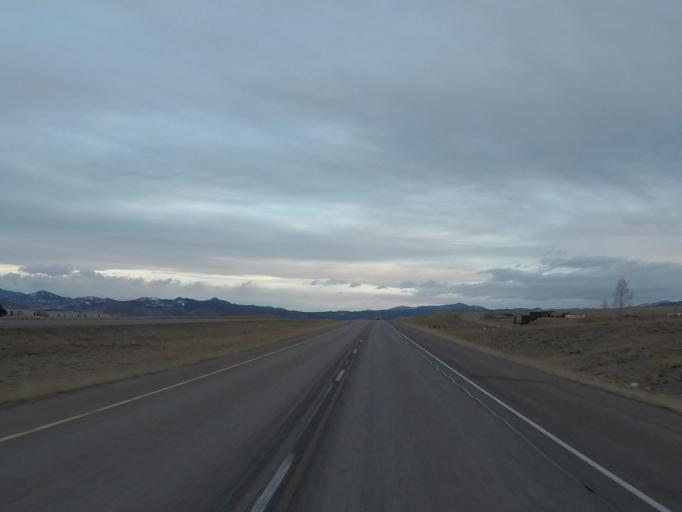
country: US
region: Montana
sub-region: Jefferson County
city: Whitehall
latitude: 45.8875
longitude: -112.1493
